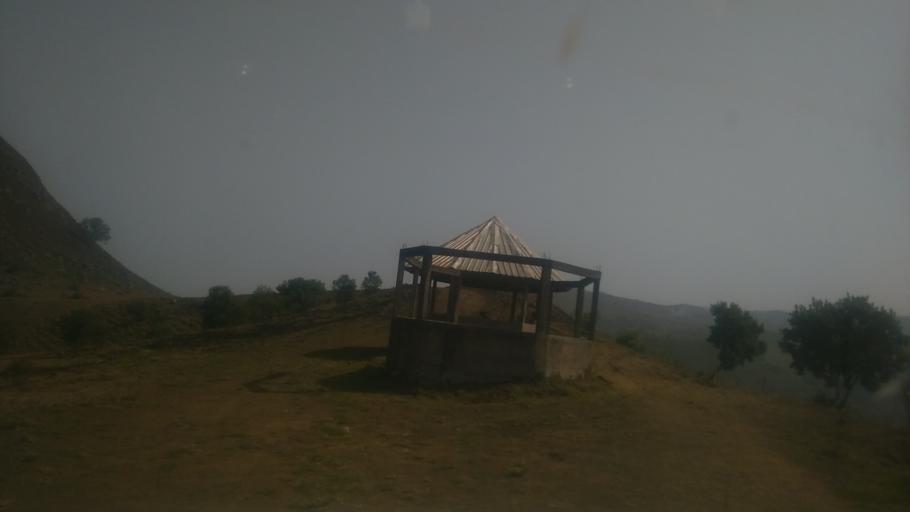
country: CM
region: Littoral
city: Nkongsamba
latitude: 5.0374
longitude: 9.8260
